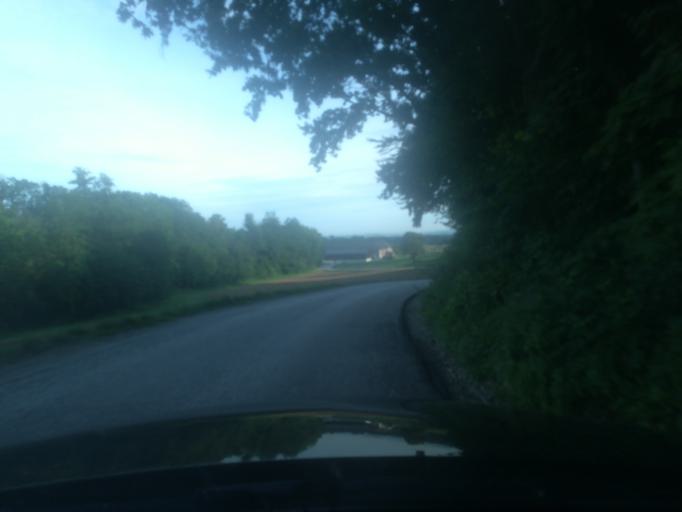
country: AT
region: Upper Austria
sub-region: Wels-Land
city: Marchtrenk
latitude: 48.1719
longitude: 14.1640
